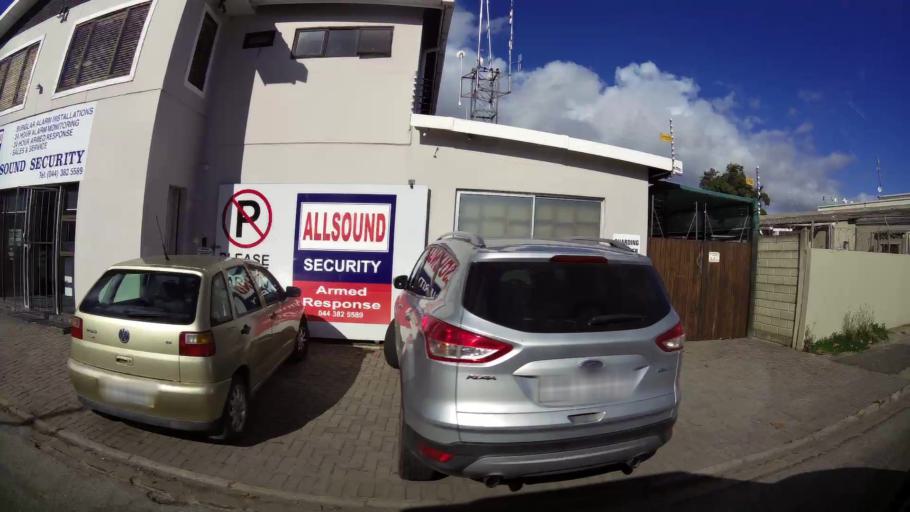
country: ZA
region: Western Cape
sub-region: Eden District Municipality
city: Knysna
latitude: -34.0376
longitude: 23.0515
